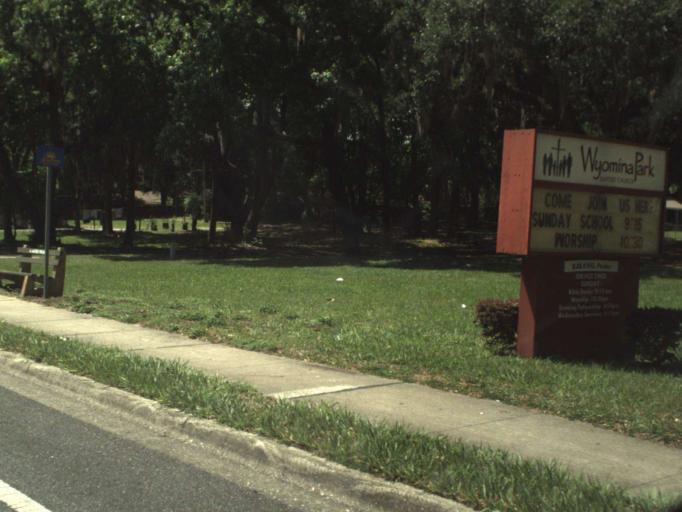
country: US
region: Florida
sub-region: Marion County
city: Ocala
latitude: 29.2007
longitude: -82.1195
